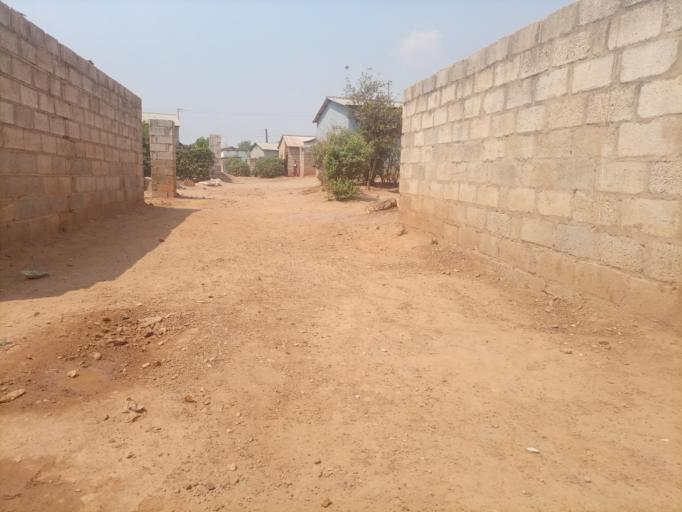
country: ZM
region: Lusaka
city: Lusaka
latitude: -15.4041
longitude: 28.3774
